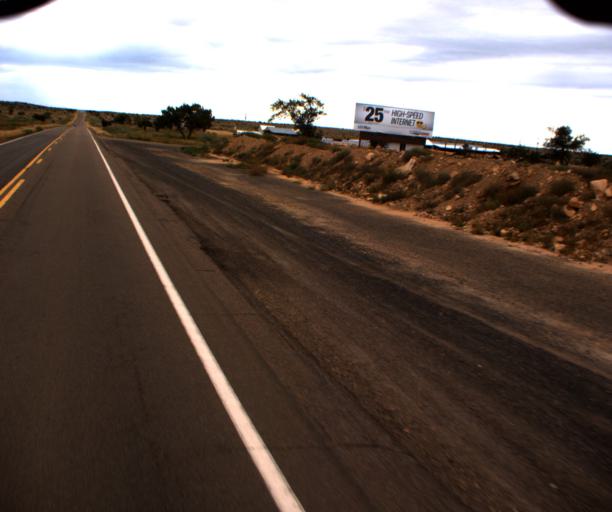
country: US
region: Arizona
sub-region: Navajo County
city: Snowflake
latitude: 34.5626
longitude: -110.0817
